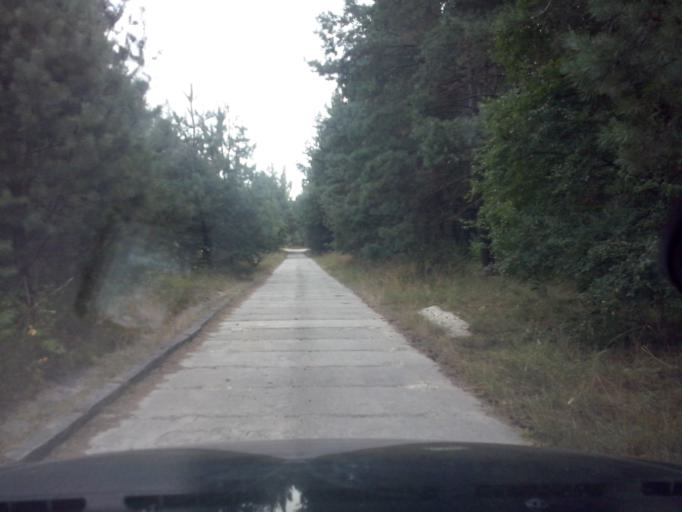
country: PL
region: Swietokrzyskie
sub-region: Powiat kielecki
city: Brzeziny
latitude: 50.7582
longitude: 20.5802
